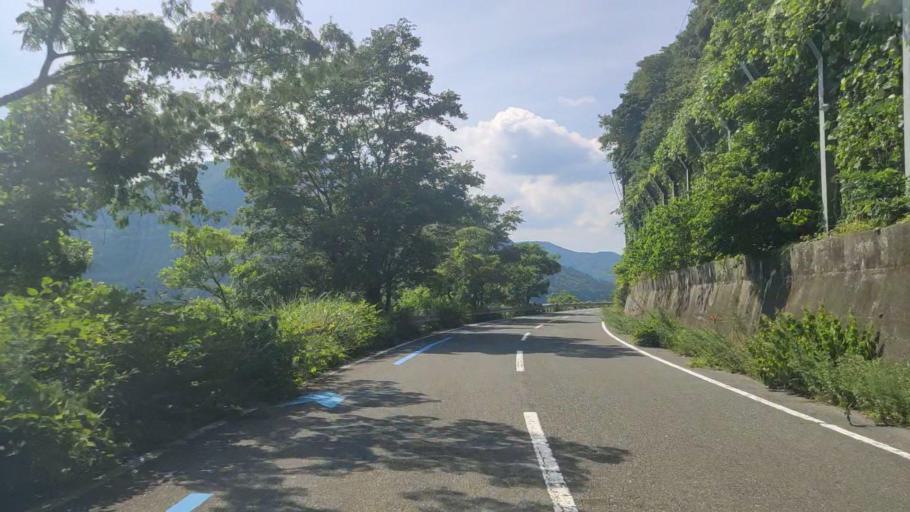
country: JP
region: Shiga Prefecture
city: Nagahama
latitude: 35.5018
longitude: 136.1710
